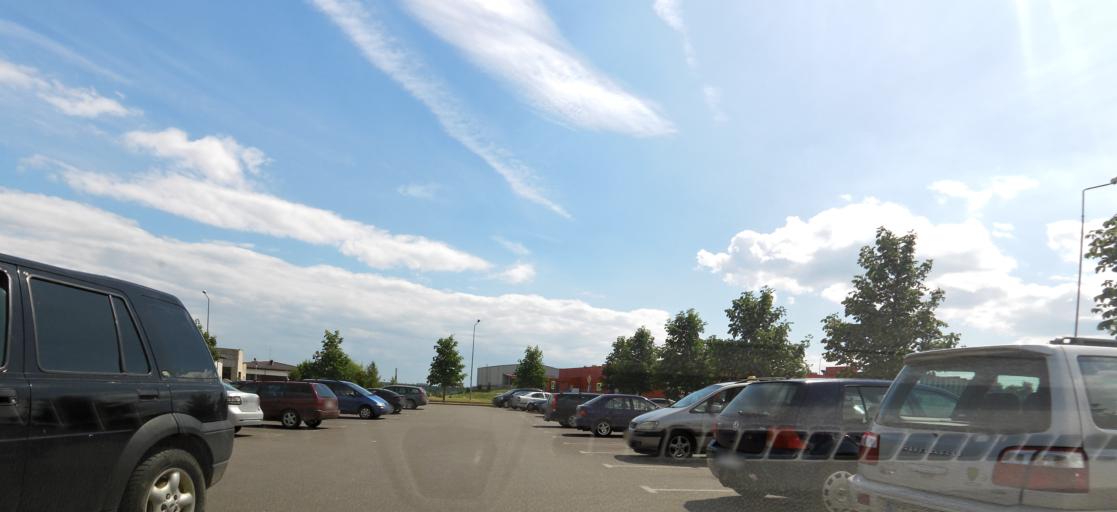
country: LT
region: Vilnius County
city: Ukmerge
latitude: 55.2426
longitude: 24.7438
